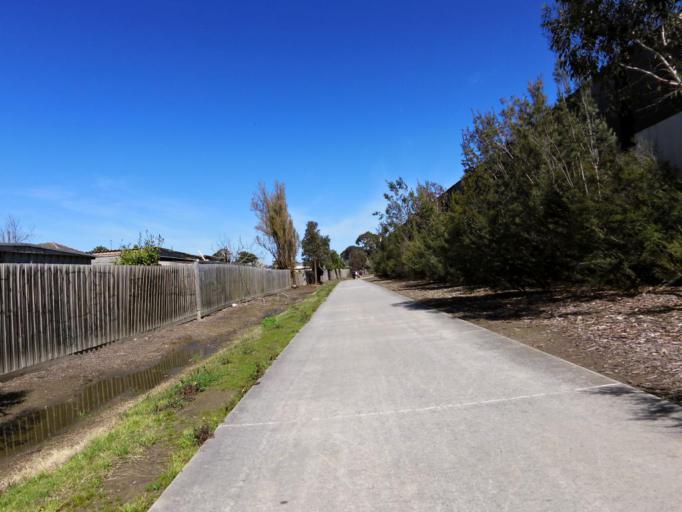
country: AU
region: Victoria
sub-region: Greater Dandenong
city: Dandenong North
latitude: -37.9580
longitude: 145.2019
